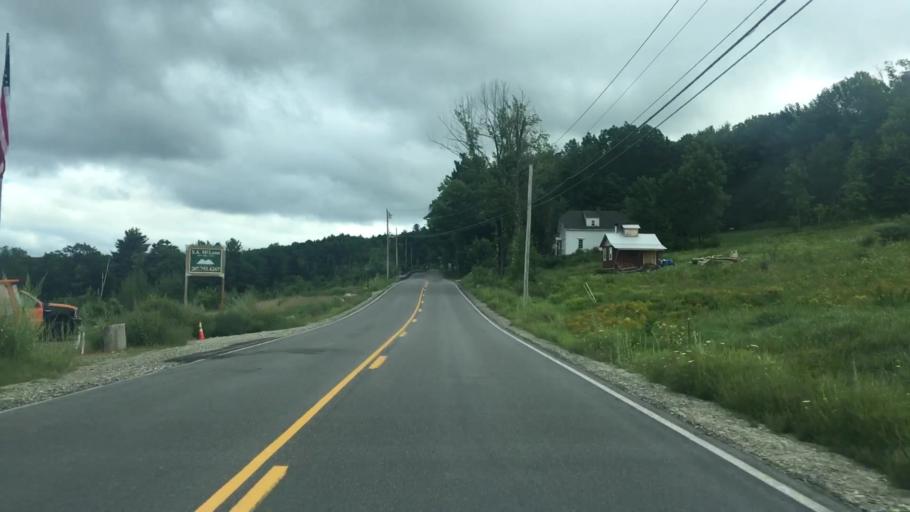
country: US
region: Maine
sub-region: York County
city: Limerick
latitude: 43.6959
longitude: -70.7998
